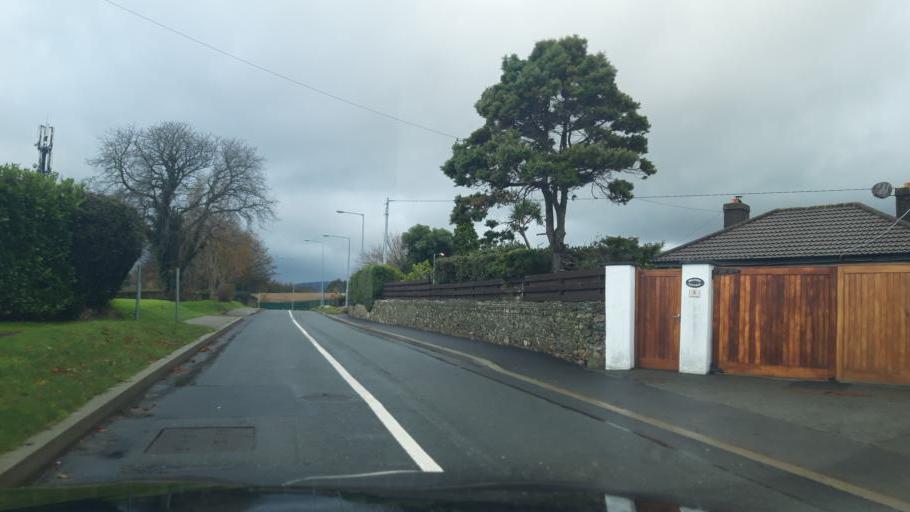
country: IE
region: Leinster
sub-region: Wicklow
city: Kilcoole
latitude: 53.1029
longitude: -6.0690
